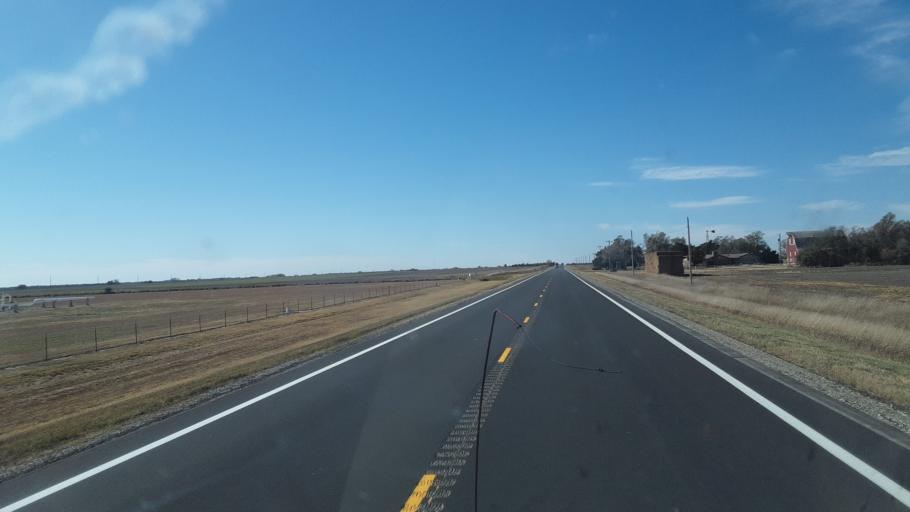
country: US
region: Kansas
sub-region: Rice County
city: Lyons
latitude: 38.3765
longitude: -98.0787
